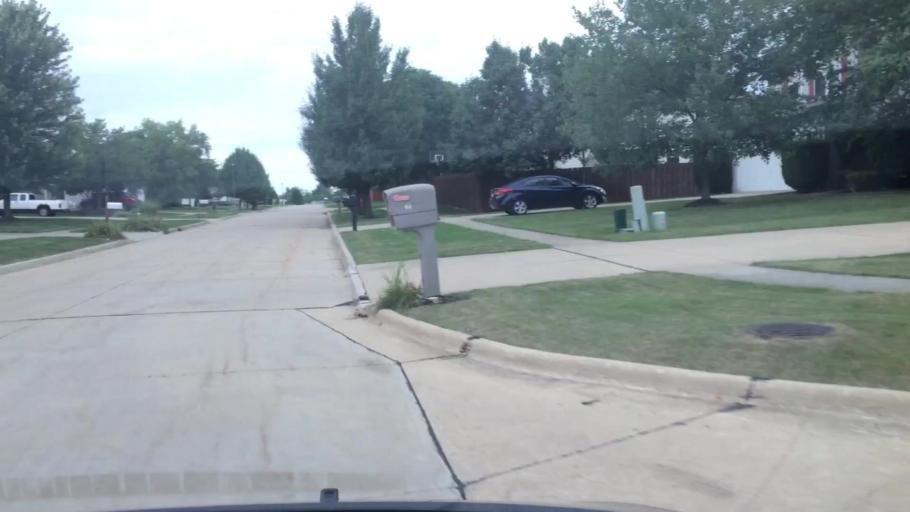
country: US
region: Ohio
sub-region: Medina County
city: Brunswick
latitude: 41.2711
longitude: -81.8174
